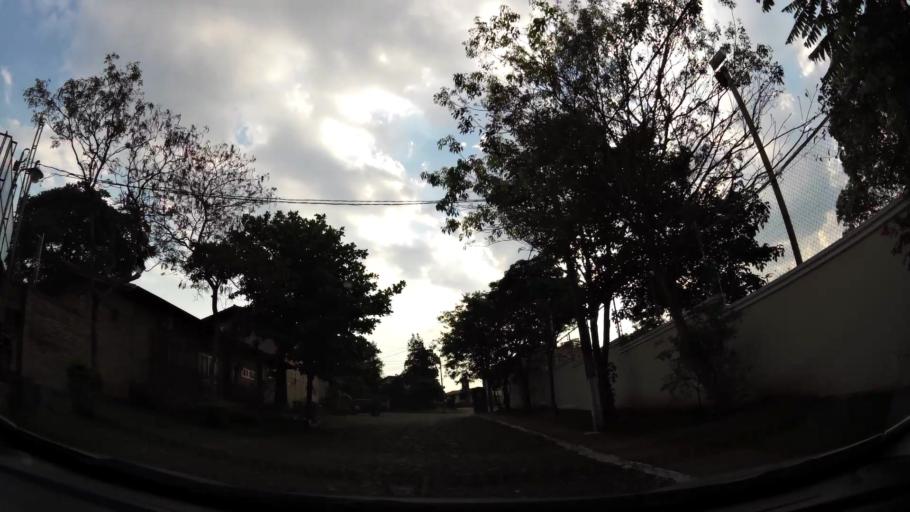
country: PY
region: Alto Parana
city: Ciudad del Este
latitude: -25.5177
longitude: -54.6283
